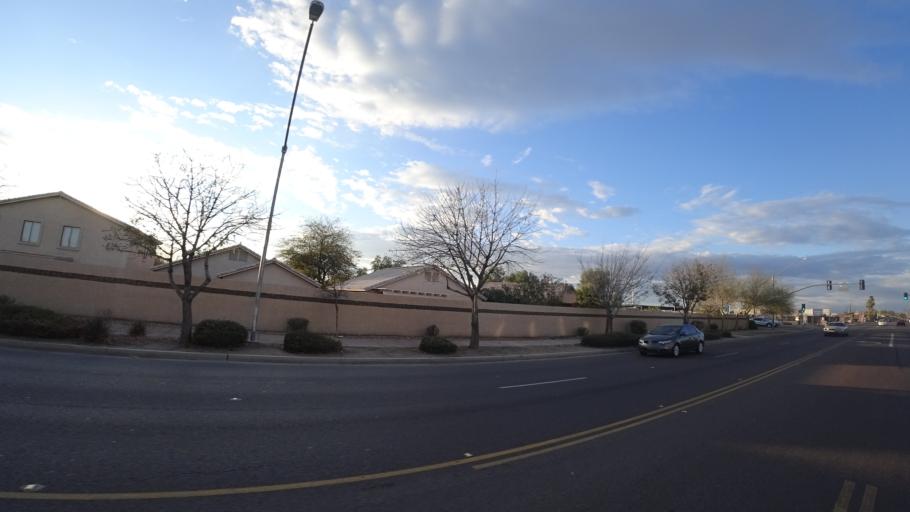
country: US
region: Arizona
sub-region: Maricopa County
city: Glendale
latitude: 33.5448
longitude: -112.2030
